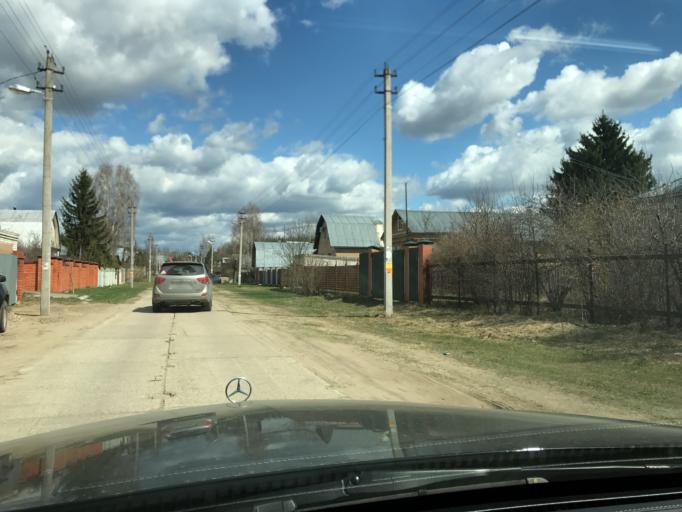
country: RU
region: Vladimir
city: Pokrov
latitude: 55.8554
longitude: 39.2003
